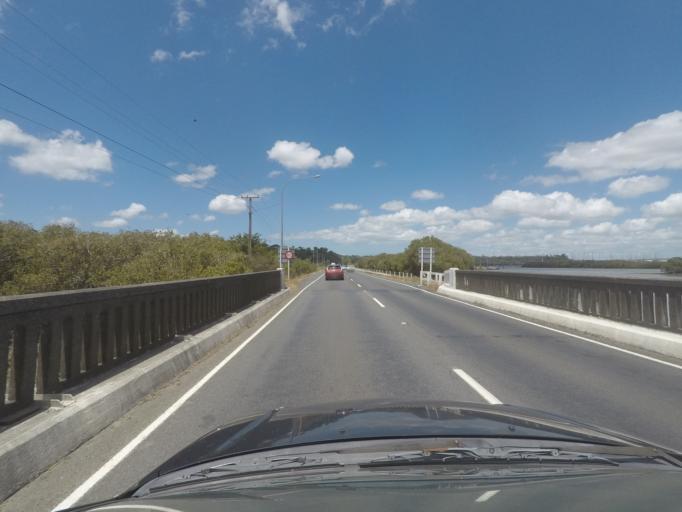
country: NZ
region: Northland
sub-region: Whangarei
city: Whangarei
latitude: -35.7321
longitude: 174.3451
